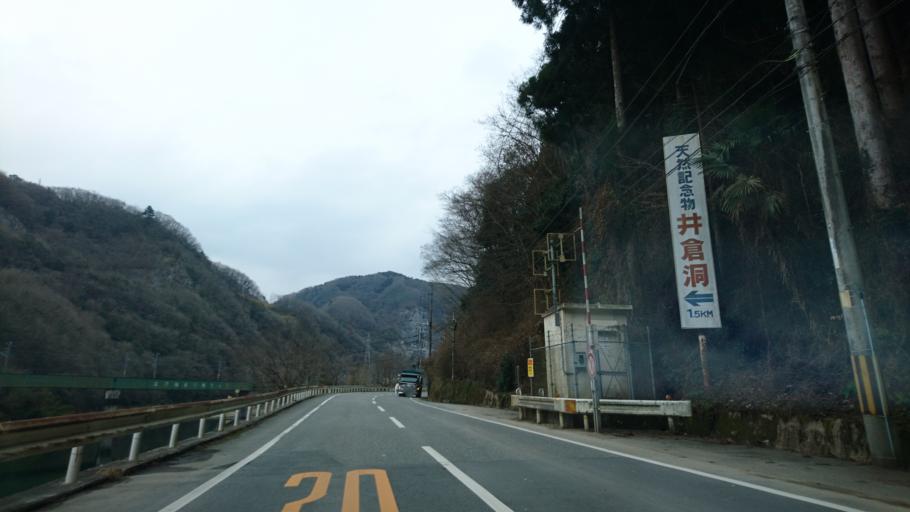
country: JP
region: Okayama
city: Niimi
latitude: 34.9296
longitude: 133.5088
